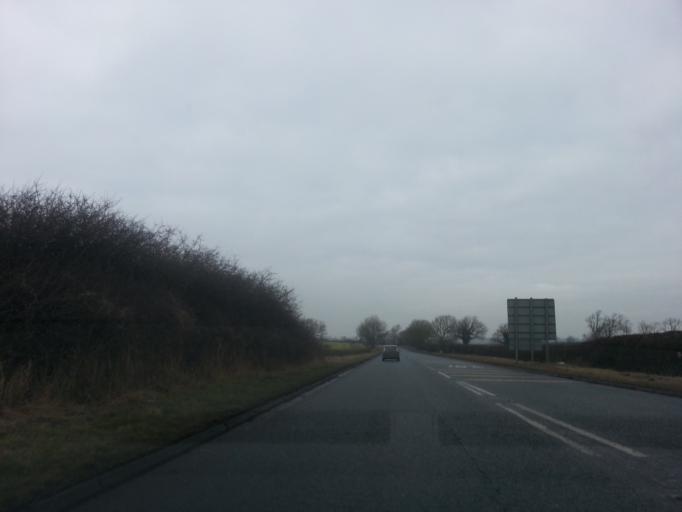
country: GB
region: England
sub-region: Darlington
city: Heighington
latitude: 54.5783
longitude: -1.6166
